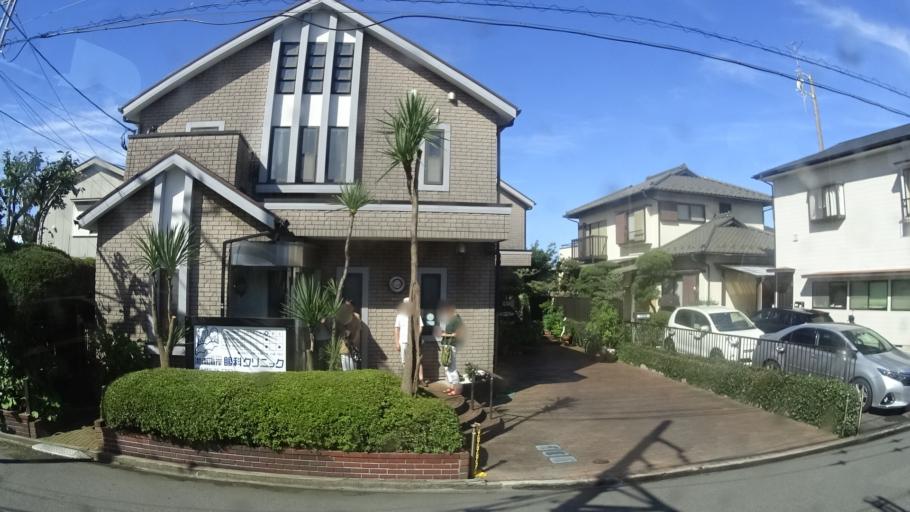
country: JP
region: Kanagawa
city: Fujisawa
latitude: 35.3141
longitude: 139.4842
